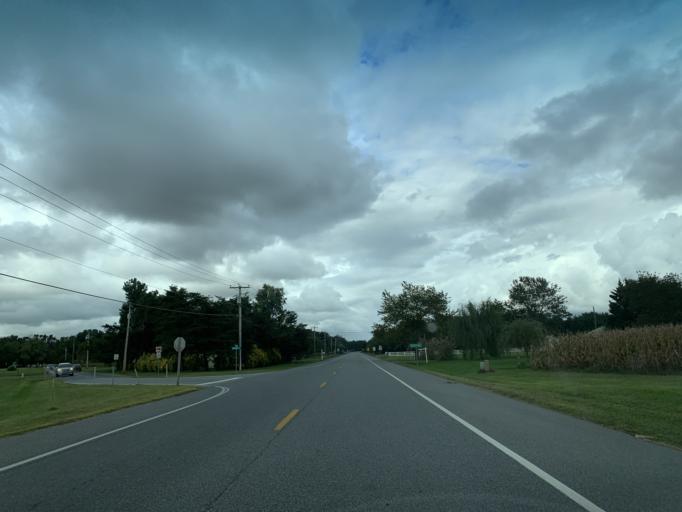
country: US
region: Maryland
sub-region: Caroline County
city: Ridgely
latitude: 39.0297
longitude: -75.8752
